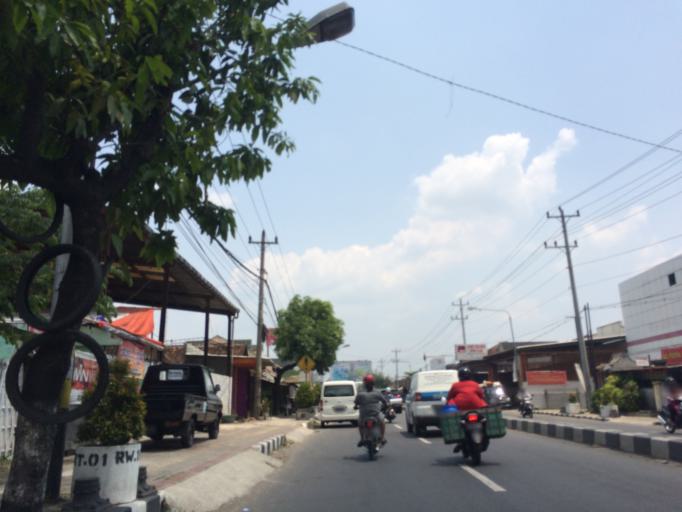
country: ID
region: Central Java
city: Grogol
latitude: -7.6168
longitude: 110.8197
